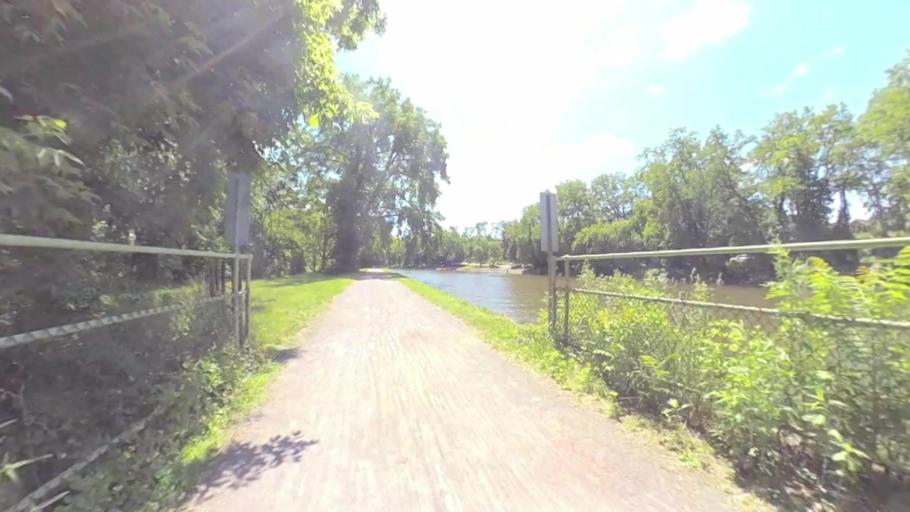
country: US
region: New York
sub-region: Monroe County
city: Pittsford
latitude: 43.0638
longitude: -77.4840
